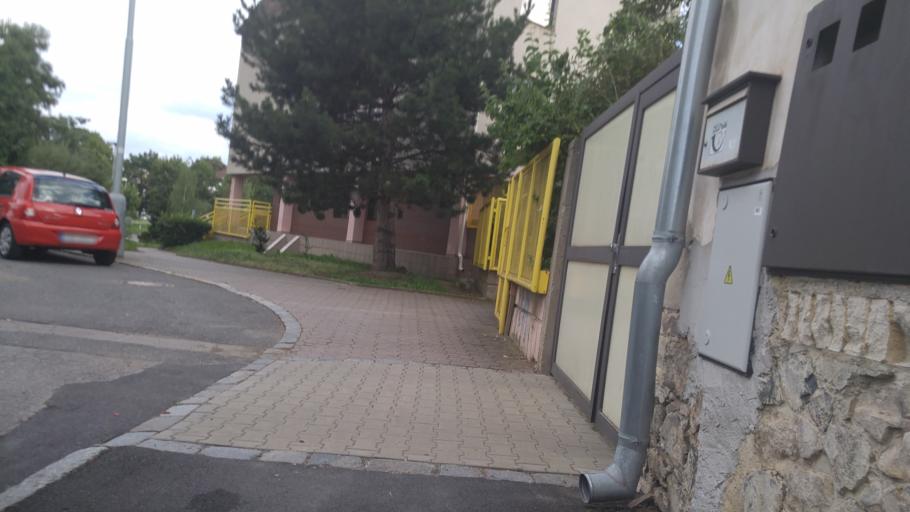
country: CZ
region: Central Bohemia
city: Horomerice
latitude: 50.0966
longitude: 14.3444
